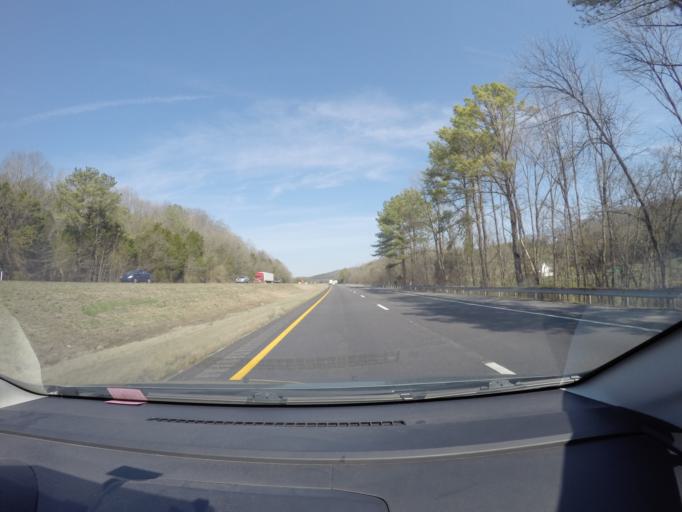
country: US
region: Tennessee
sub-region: Rutherford County
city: Plainview
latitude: 35.6352
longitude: -86.2473
